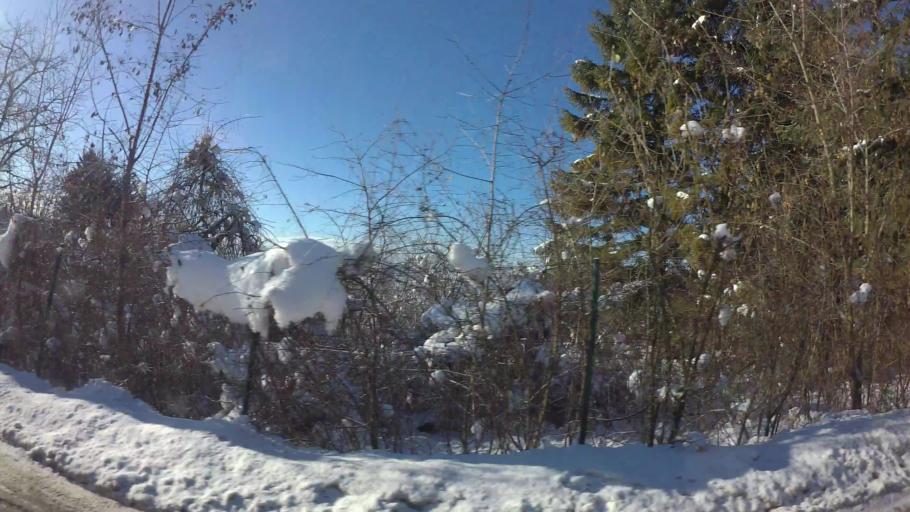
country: BA
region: Federation of Bosnia and Herzegovina
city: Kobilja Glava
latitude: 43.8871
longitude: 18.4093
